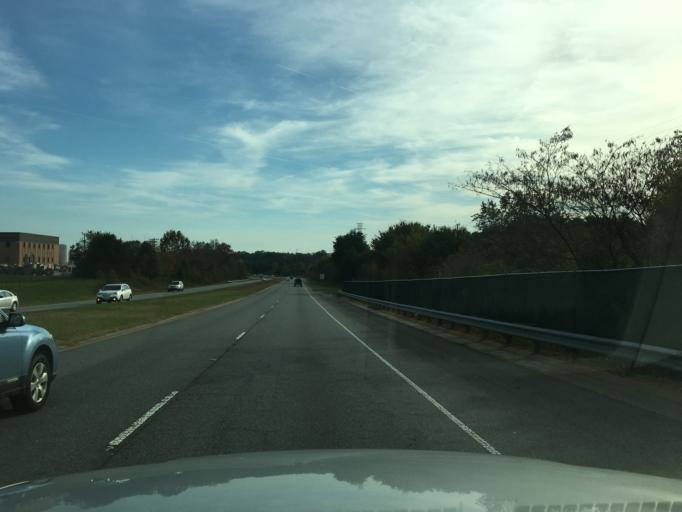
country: US
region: North Carolina
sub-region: Catawba County
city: Hickory
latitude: 35.7157
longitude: -81.2949
